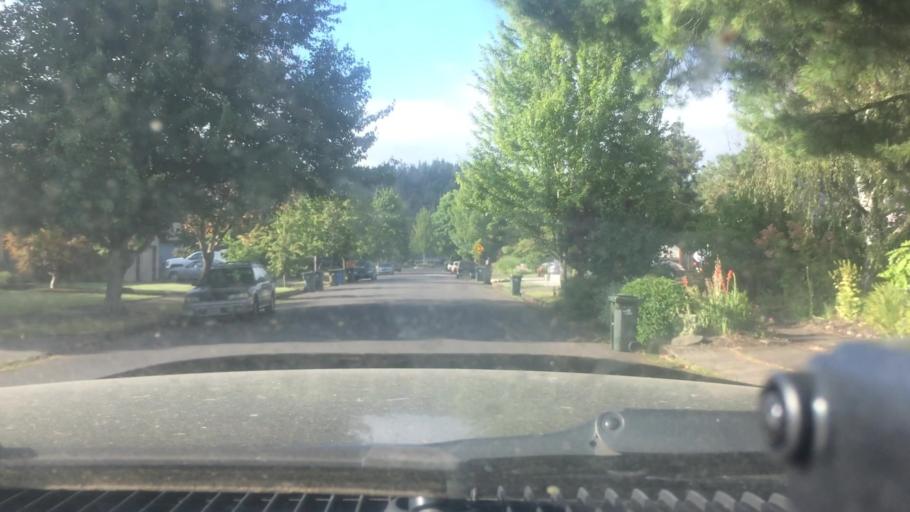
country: US
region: Oregon
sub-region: Lane County
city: Eugene
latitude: 44.0313
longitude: -123.1112
